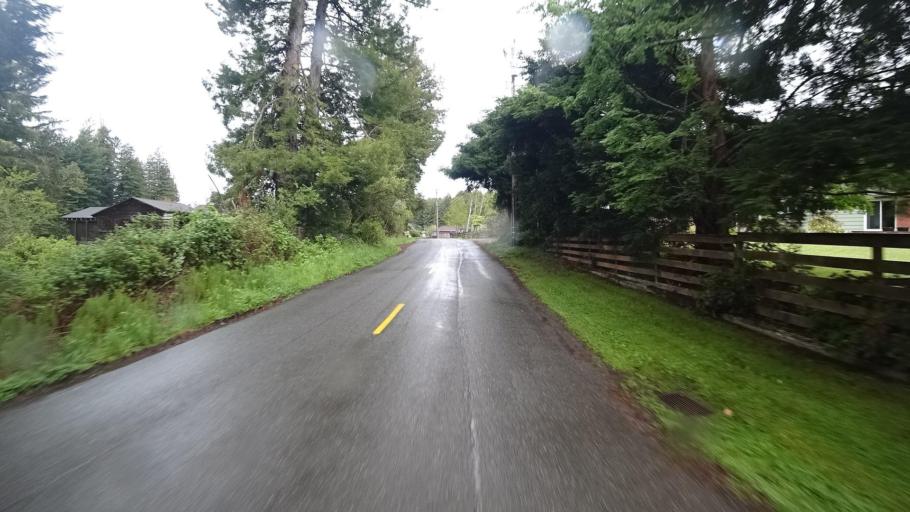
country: US
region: California
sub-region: Humboldt County
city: Bayside
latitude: 40.8299
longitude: -124.0395
